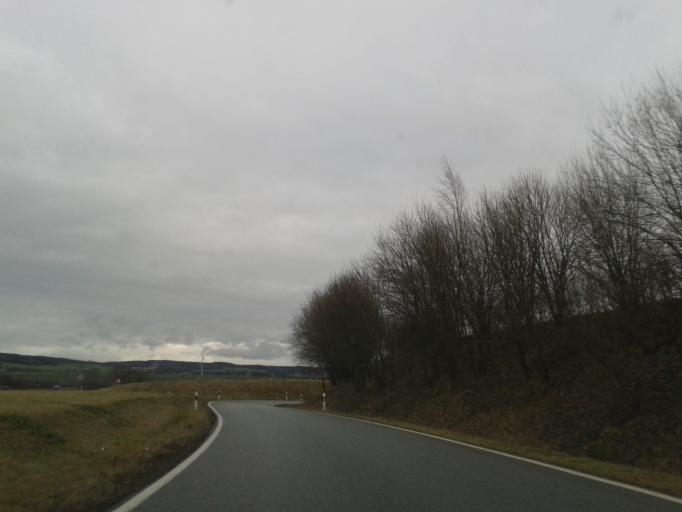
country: DE
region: Saxony
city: Lobau
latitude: 51.0804
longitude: 14.6537
